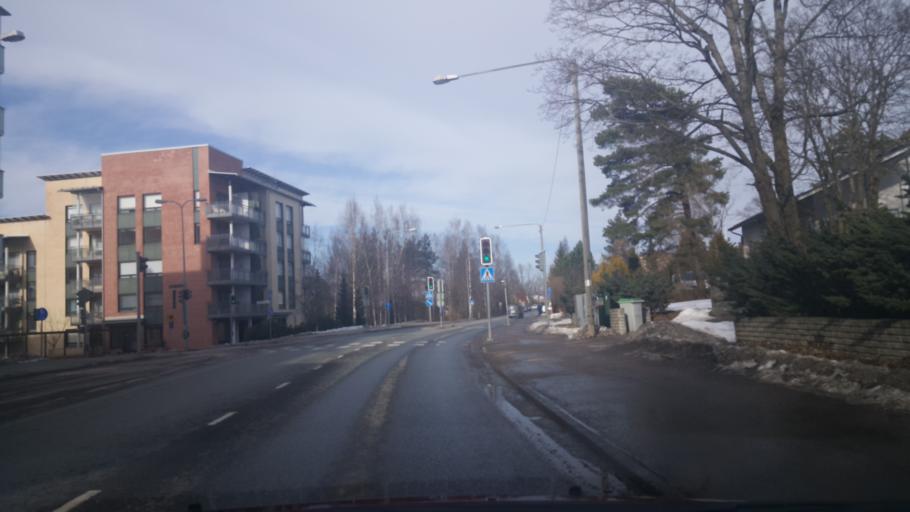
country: FI
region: Uusimaa
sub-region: Helsinki
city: Teekkarikylae
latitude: 60.2571
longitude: 24.8722
